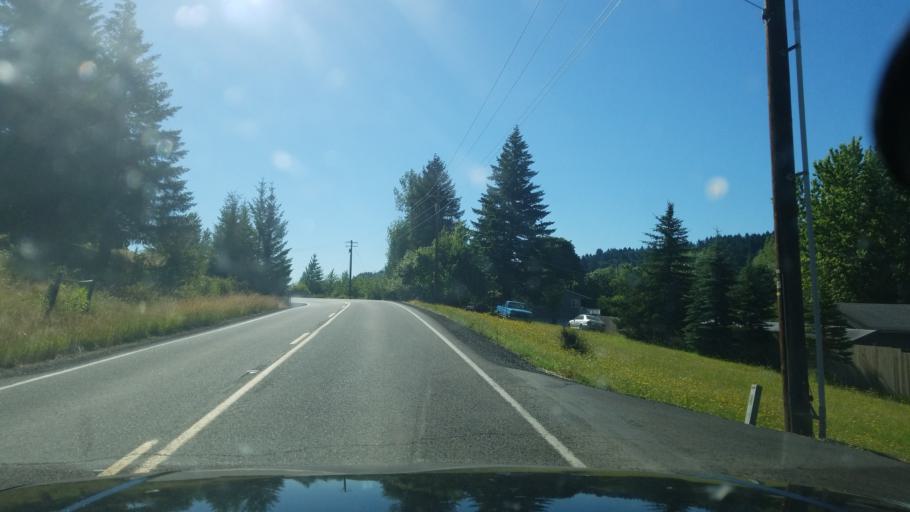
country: US
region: Oregon
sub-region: Yamhill County
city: McMinnville
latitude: 45.2251
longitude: -123.2618
